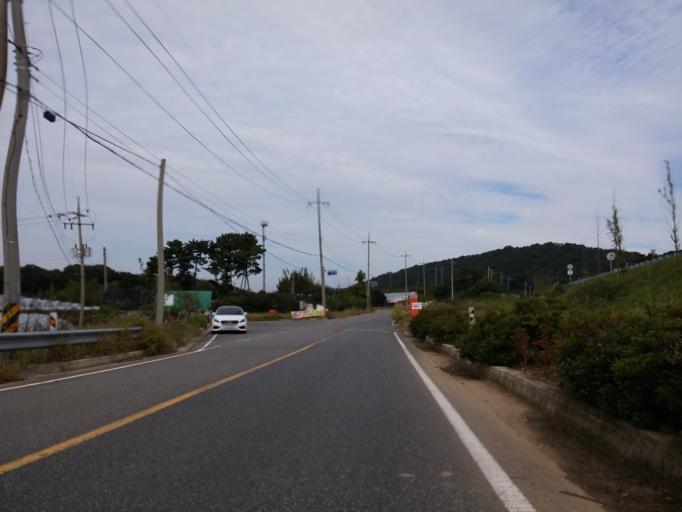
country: KR
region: Chungcheongnam-do
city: Yonmu
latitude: 36.1630
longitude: 127.1824
